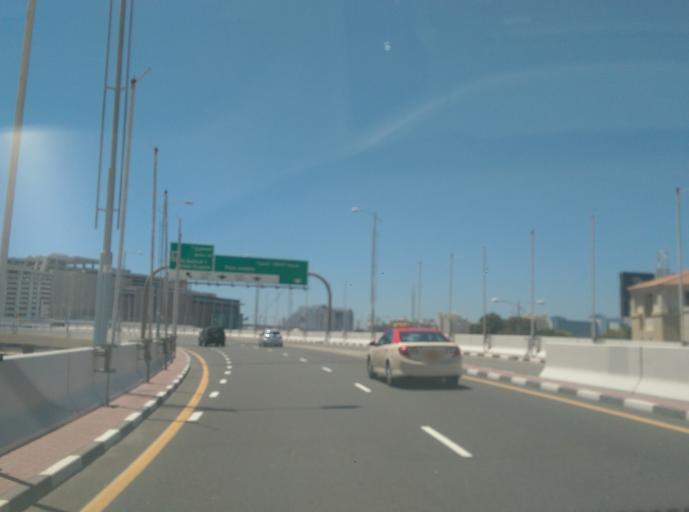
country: AE
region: Dubai
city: Dubai
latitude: 25.1008
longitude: 55.1607
